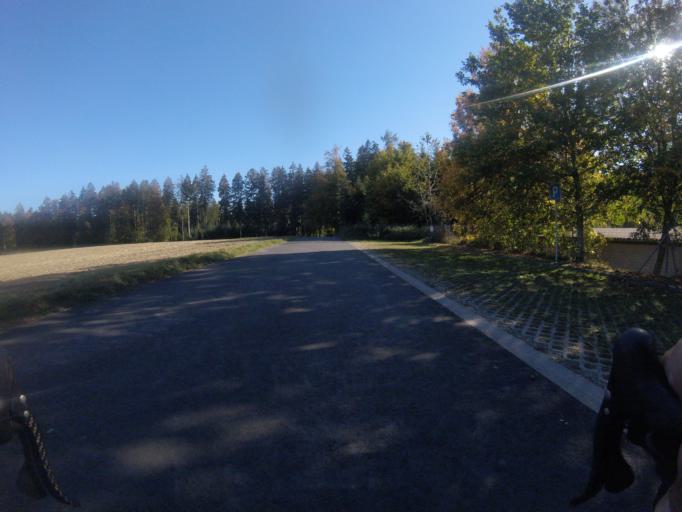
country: CH
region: Bern
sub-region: Bern-Mittelland District
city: Kirchlindach
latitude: 47.0097
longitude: 7.4070
